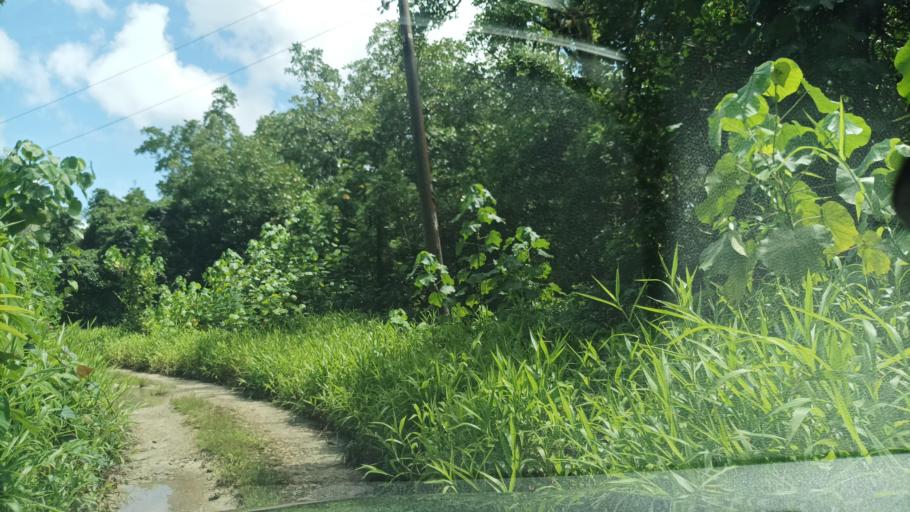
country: FM
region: Pohnpei
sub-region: Sokehs Municipality
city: Palikir - National Government Center
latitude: 6.9468
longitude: 158.1596
